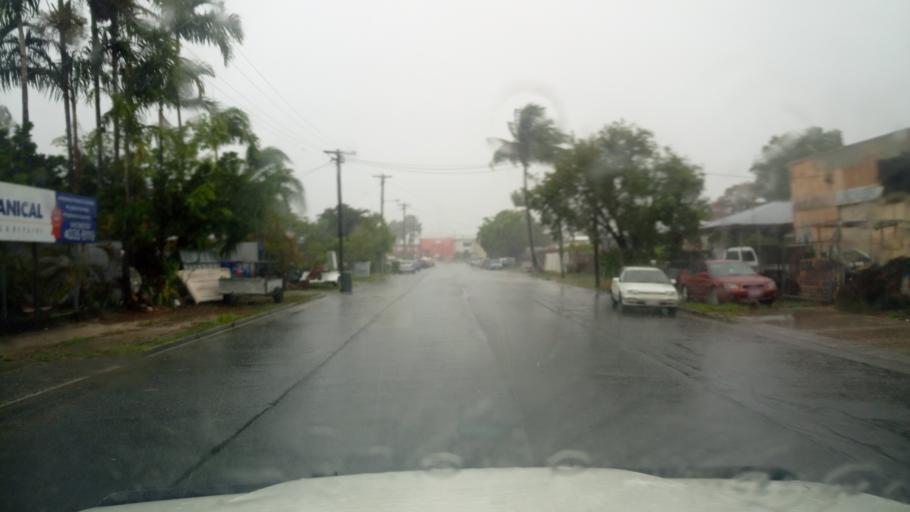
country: AU
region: Queensland
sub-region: Cairns
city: Woree
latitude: -16.9382
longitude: 145.7605
